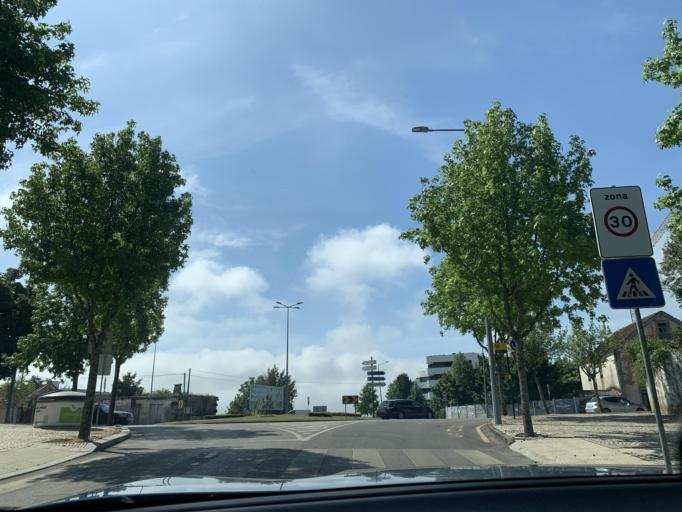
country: PT
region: Viseu
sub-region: Viseu
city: Viseu
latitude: 40.6536
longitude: -7.9085
